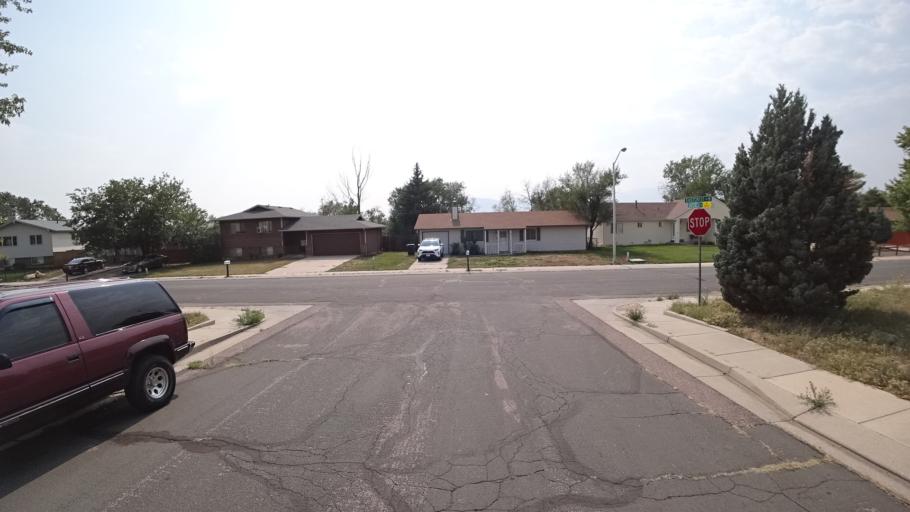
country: US
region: Colorado
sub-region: El Paso County
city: Cimarron Hills
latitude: 38.8313
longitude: -104.7466
